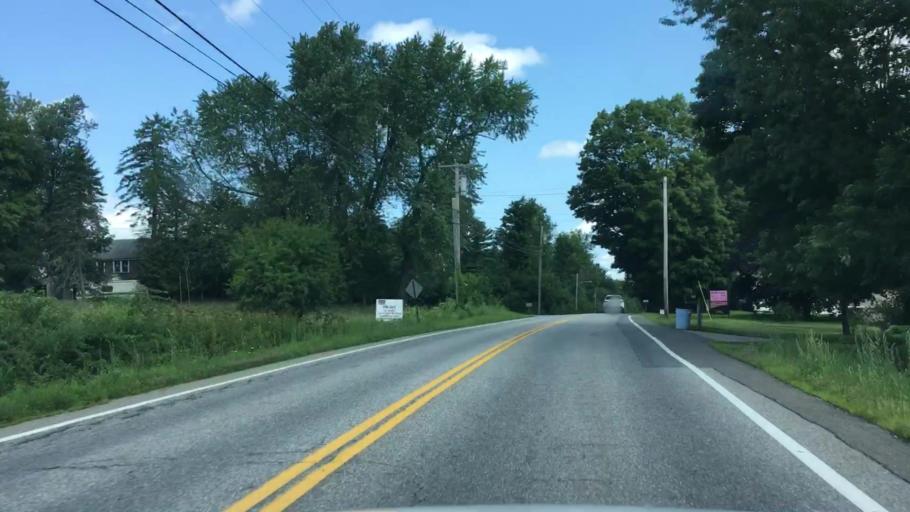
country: US
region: Maine
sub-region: Kennebec County
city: Augusta
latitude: 44.3308
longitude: -69.8172
